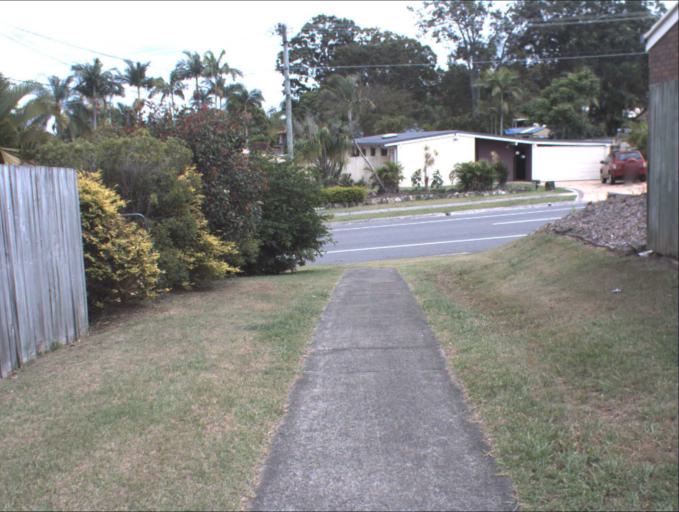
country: AU
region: Queensland
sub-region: Logan
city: Slacks Creek
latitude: -27.6299
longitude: 153.1440
